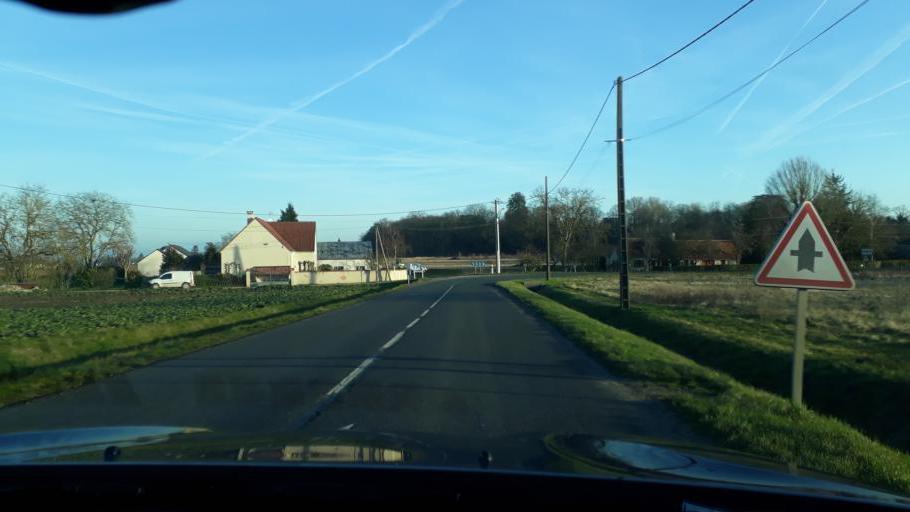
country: FR
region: Centre
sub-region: Departement du Loiret
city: Neuville-aux-Bois
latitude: 48.0509
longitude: 2.0519
